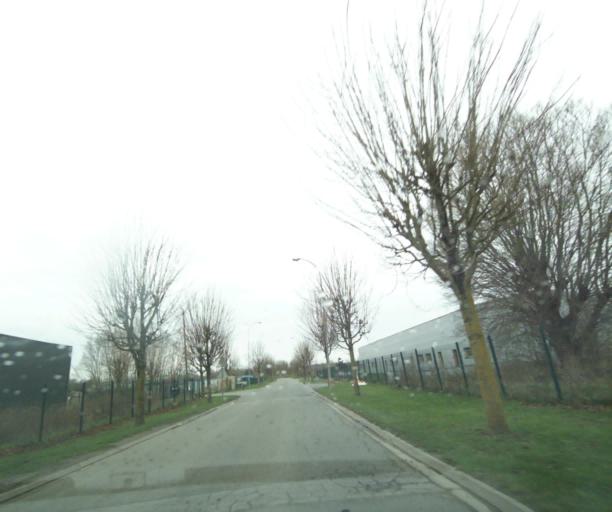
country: FR
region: Nord-Pas-de-Calais
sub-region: Departement du Nord
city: Fresnes-sur-Escaut
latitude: 50.4114
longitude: 3.5752
